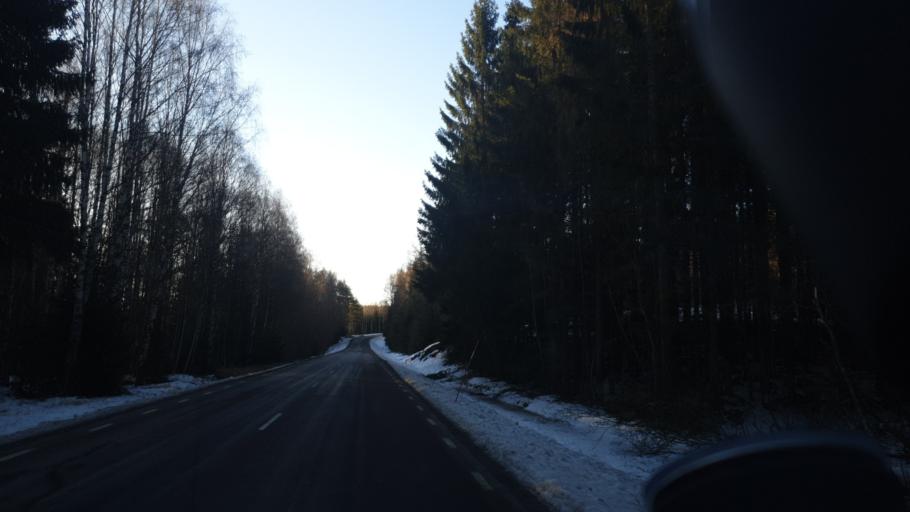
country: SE
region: Vaermland
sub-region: Eda Kommun
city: Charlottenberg
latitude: 59.7915
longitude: 12.2556
